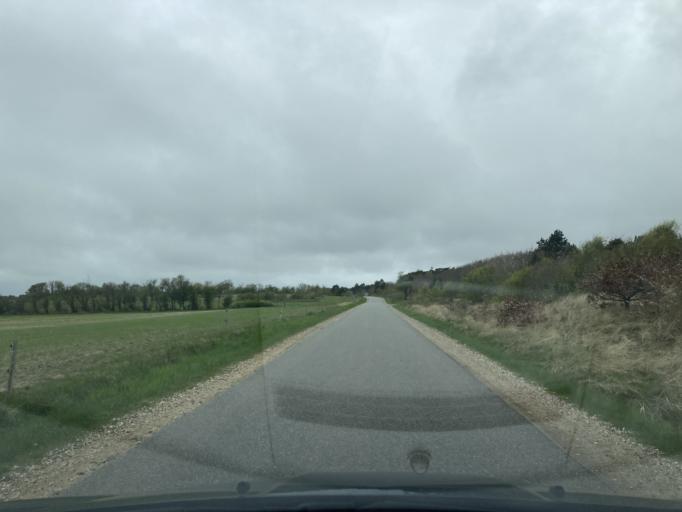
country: DK
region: North Denmark
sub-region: Thisted Kommune
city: Hurup
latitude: 56.8146
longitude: 8.3143
